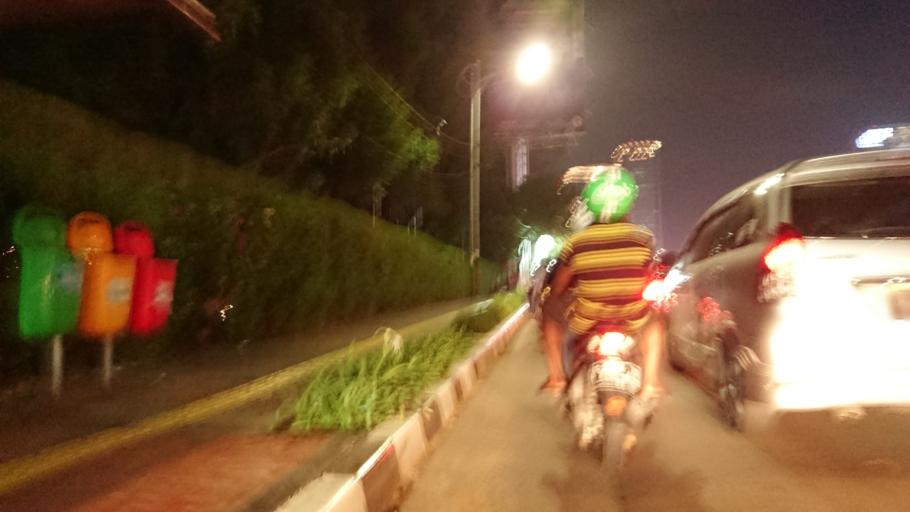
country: ID
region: Jakarta Raya
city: Jakarta
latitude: -6.2064
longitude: 106.8019
